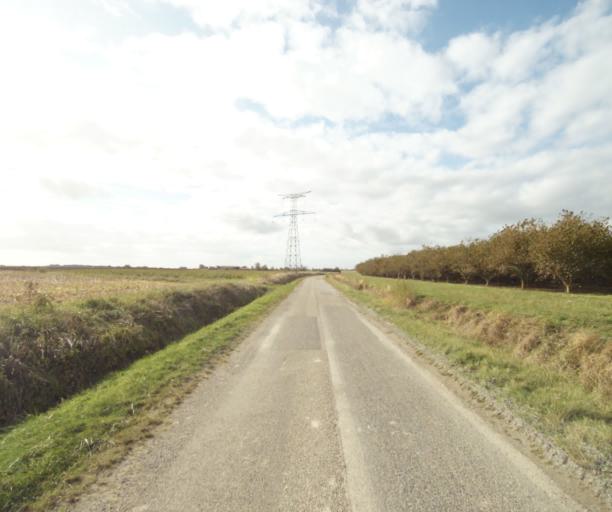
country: FR
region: Midi-Pyrenees
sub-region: Departement du Tarn-et-Garonne
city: Finhan
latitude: 43.8993
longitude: 1.1201
